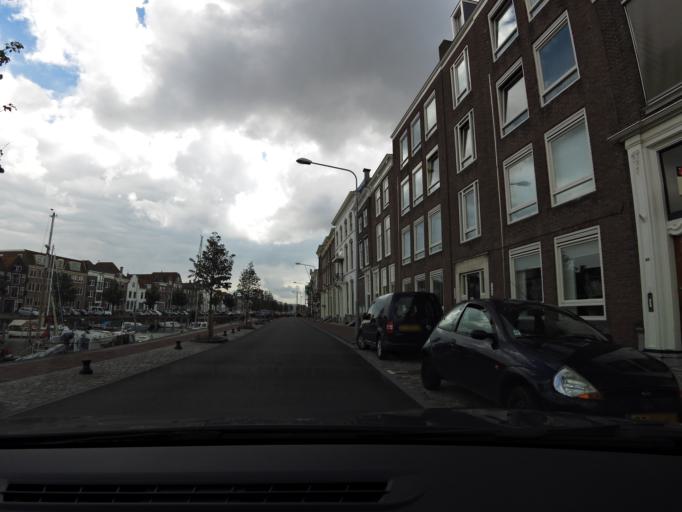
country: NL
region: Zeeland
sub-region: Gemeente Middelburg
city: Middelburg
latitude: 51.4999
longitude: 3.6205
